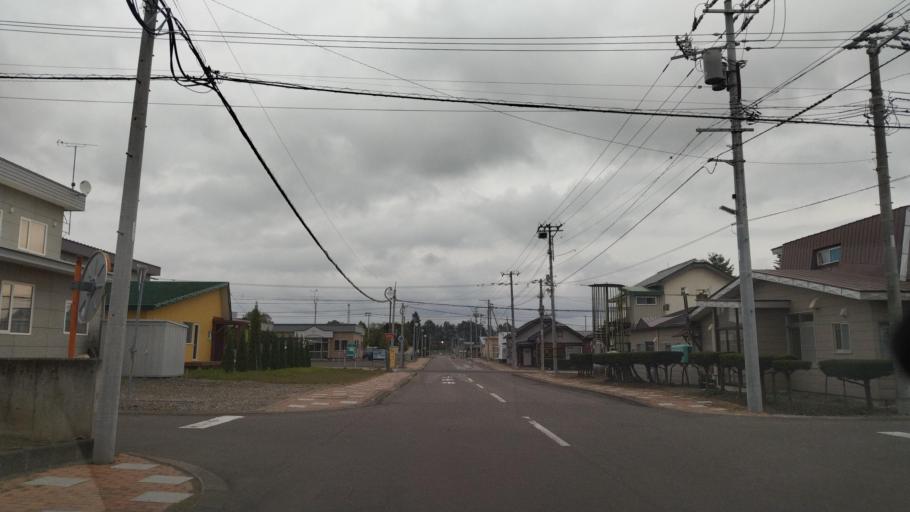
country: JP
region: Hokkaido
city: Otofuke
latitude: 43.2323
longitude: 143.2925
